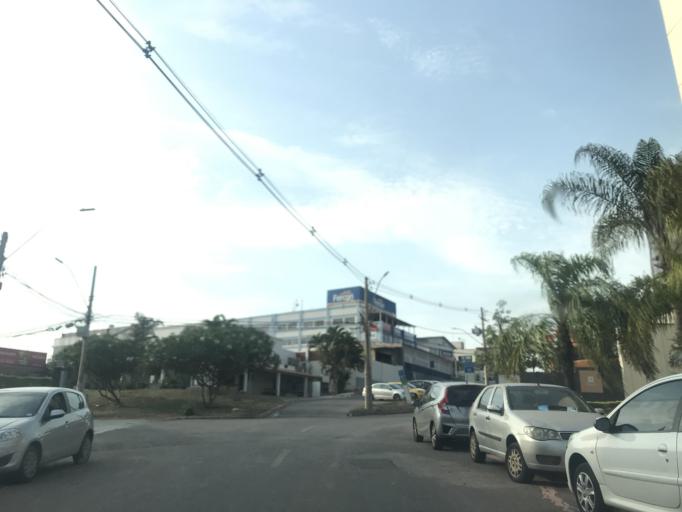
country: BR
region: Federal District
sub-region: Brasilia
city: Brasilia
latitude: -15.7157
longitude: -47.8869
